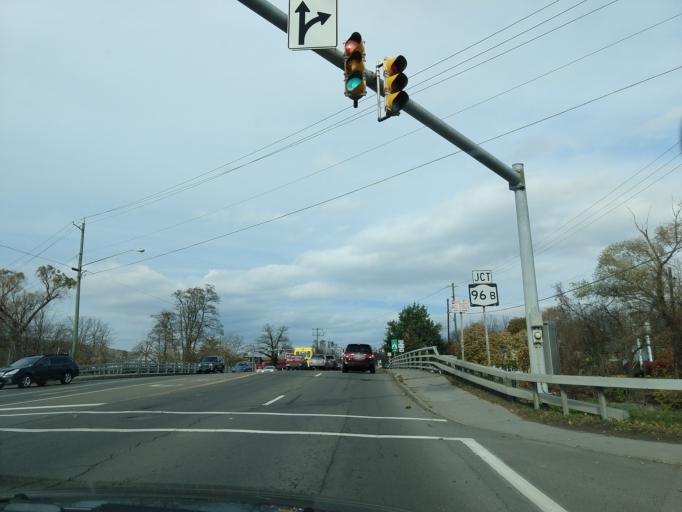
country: US
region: New York
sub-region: Tompkins County
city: Ithaca
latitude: 42.4357
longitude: -76.5082
